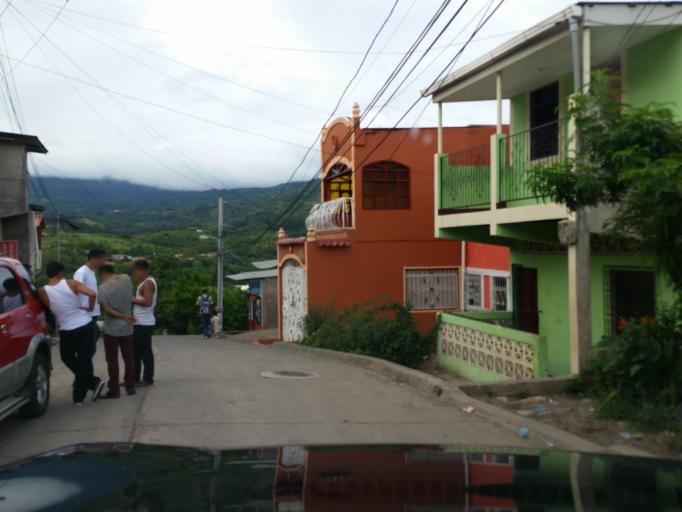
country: NI
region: Matagalpa
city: Matagalpa
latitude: 12.9327
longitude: -85.9144
